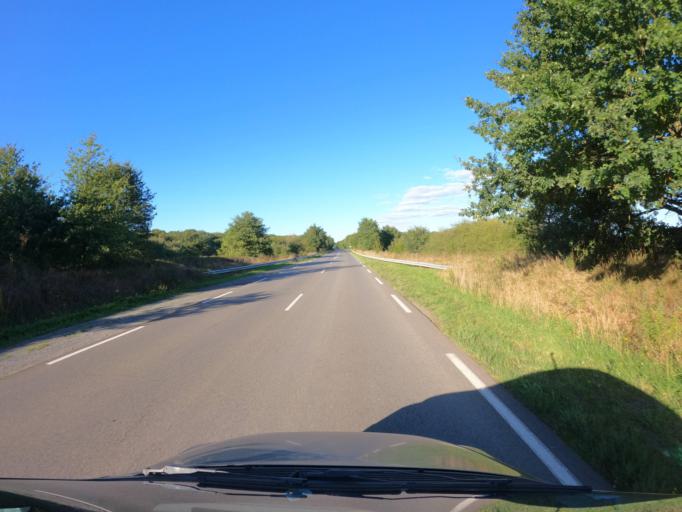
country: FR
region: Bourgogne
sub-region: Departement de Saone-et-Loire
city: Saint-Eusebe
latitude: 46.7218
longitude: 4.4311
